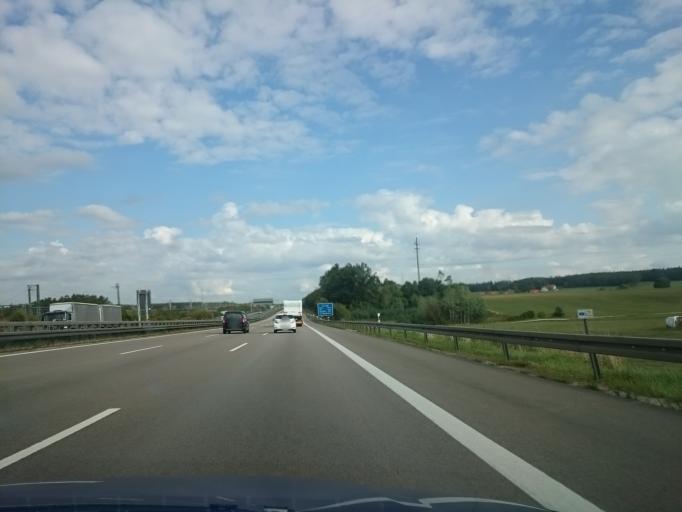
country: DE
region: Bavaria
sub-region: Regierungsbezirk Mittelfranken
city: Allersberg
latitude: 49.2552
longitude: 11.2152
